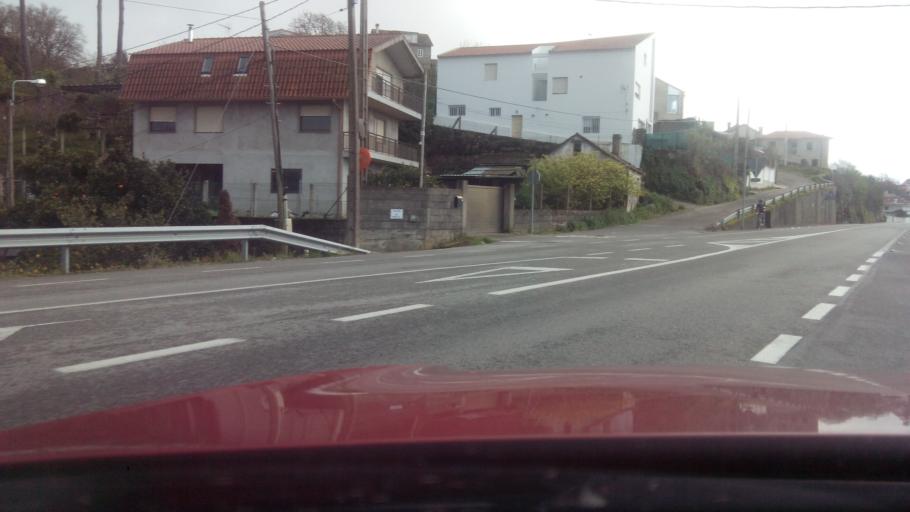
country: ES
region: Galicia
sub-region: Provincia de Pontevedra
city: Nigran
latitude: 42.1598
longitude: -8.8156
